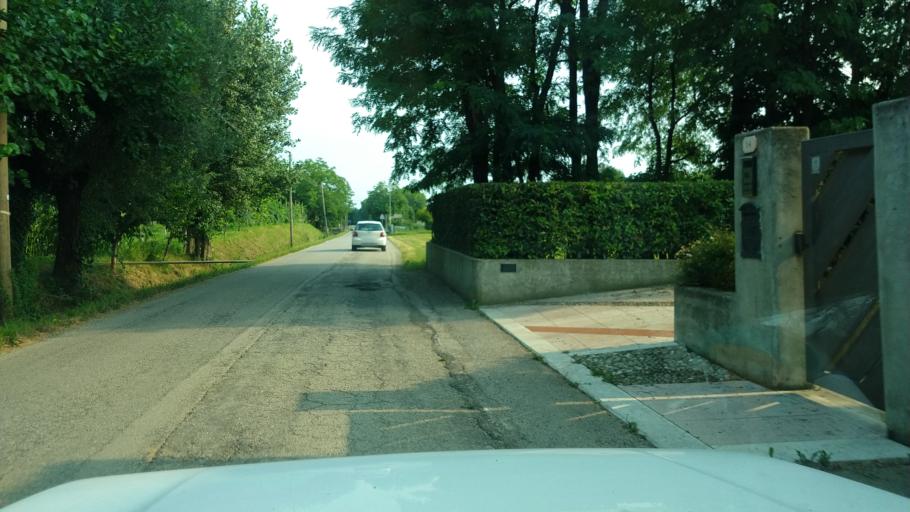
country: IT
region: Veneto
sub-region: Provincia di Vicenza
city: Nove
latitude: 45.7229
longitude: 11.6576
